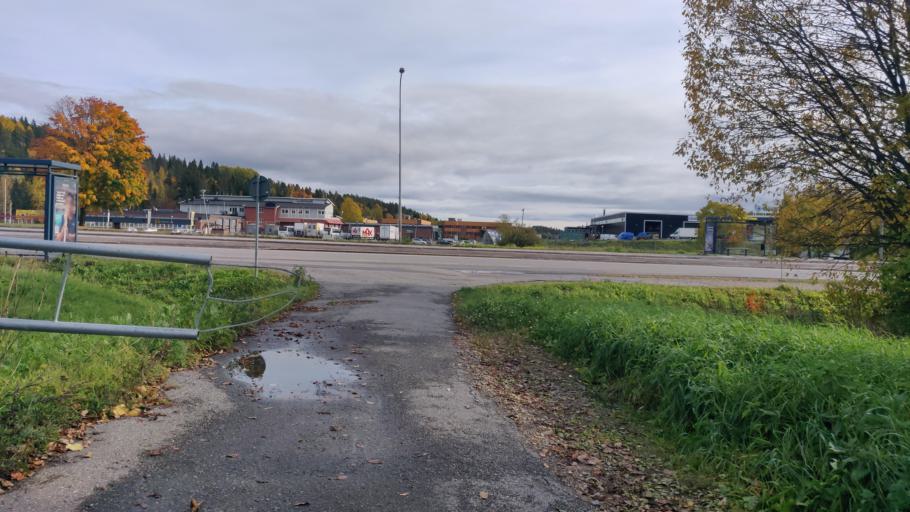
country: SE
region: Vaesternorrland
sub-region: Sundsvalls Kommun
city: Johannedal
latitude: 62.4167
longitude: 17.3415
